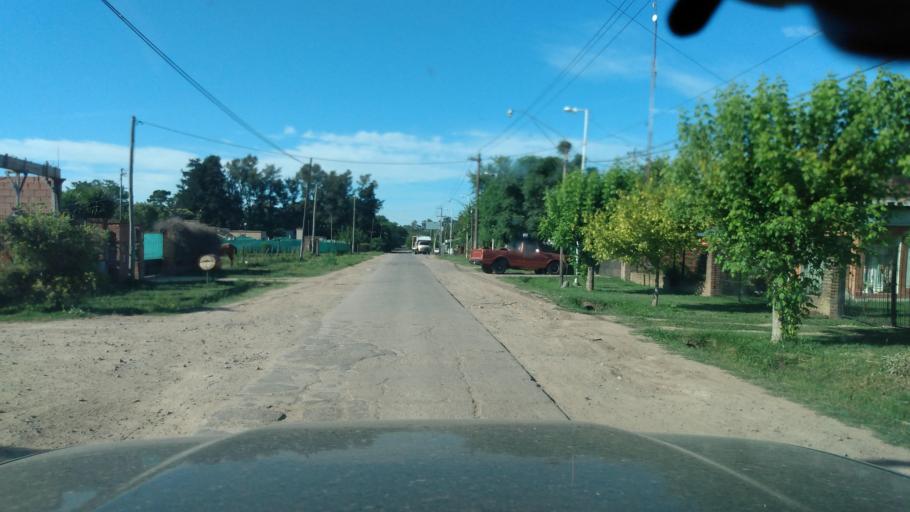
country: AR
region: Buenos Aires
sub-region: Partido de Lujan
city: Lujan
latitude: -34.5854
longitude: -59.0580
